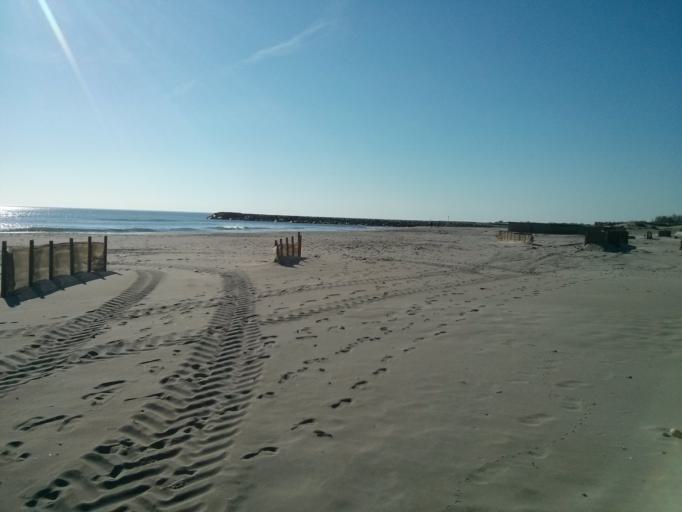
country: FR
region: Provence-Alpes-Cote d'Azur
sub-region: Departement des Bouches-du-Rhone
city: Saintes-Maries-de-la-Mer
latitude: 43.4495
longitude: 4.4182
